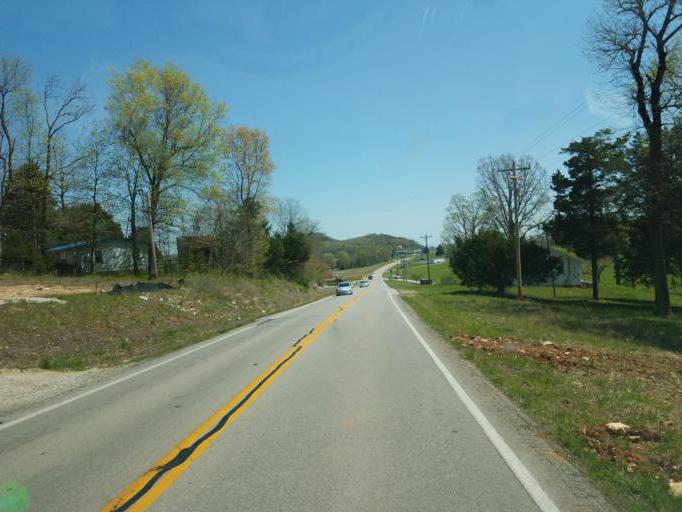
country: US
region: Kentucky
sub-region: Barren County
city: Cave City
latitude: 37.1342
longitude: -85.9975
